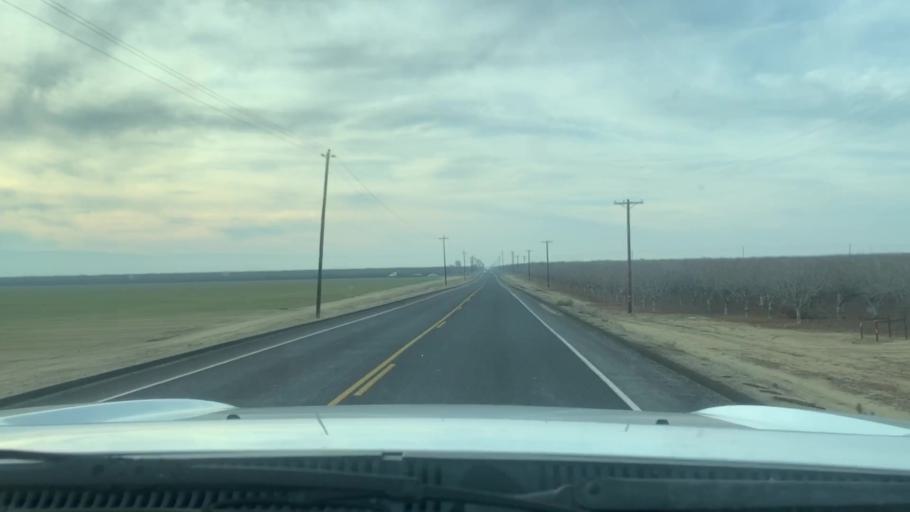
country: US
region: California
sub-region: Kern County
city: Lost Hills
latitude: 35.4993
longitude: -119.6491
